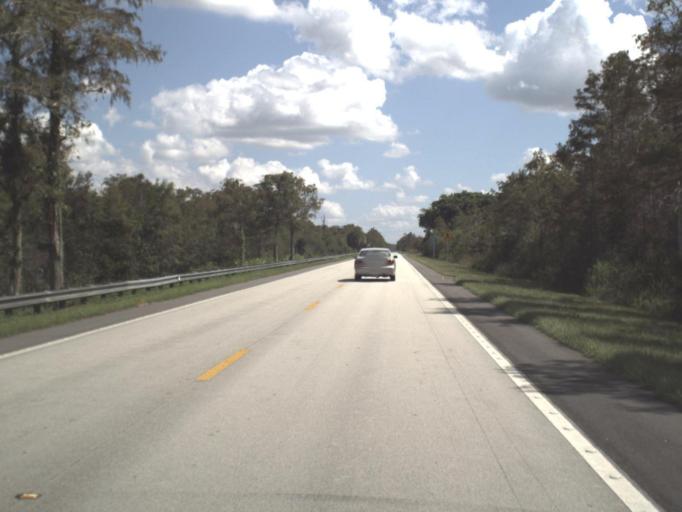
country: US
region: Florida
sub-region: Miami-Dade County
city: Kendall West
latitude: 25.8211
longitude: -80.8914
